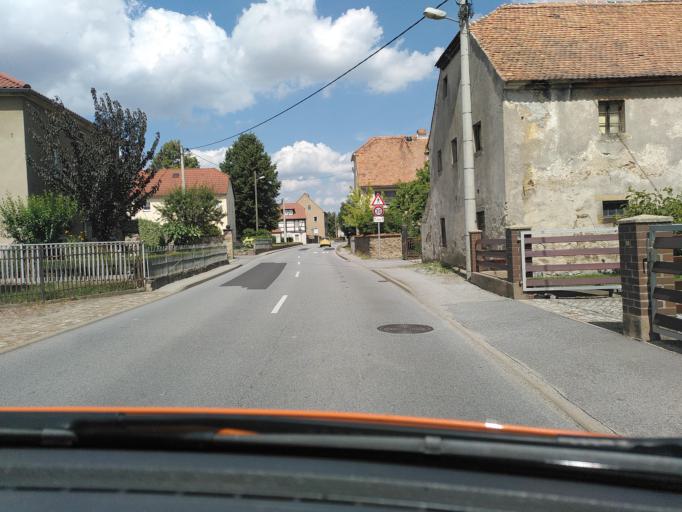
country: DE
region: Saxony
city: Grossdubrau
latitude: 51.2253
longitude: 14.4780
